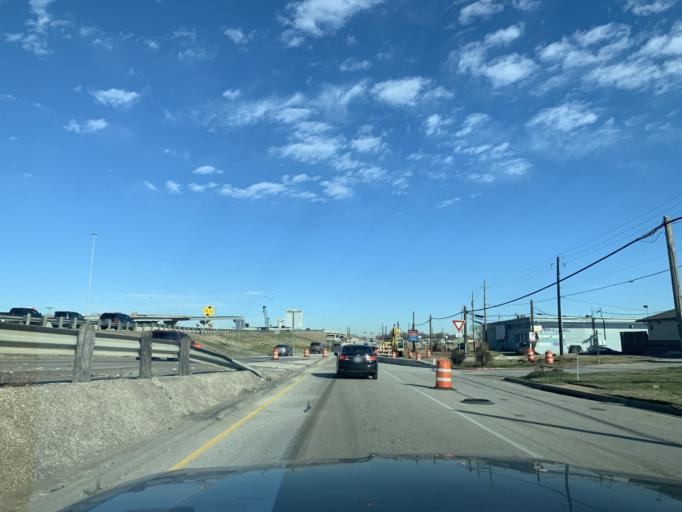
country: US
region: Texas
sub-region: Tarrant County
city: Arlington
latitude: 32.7549
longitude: -97.0629
